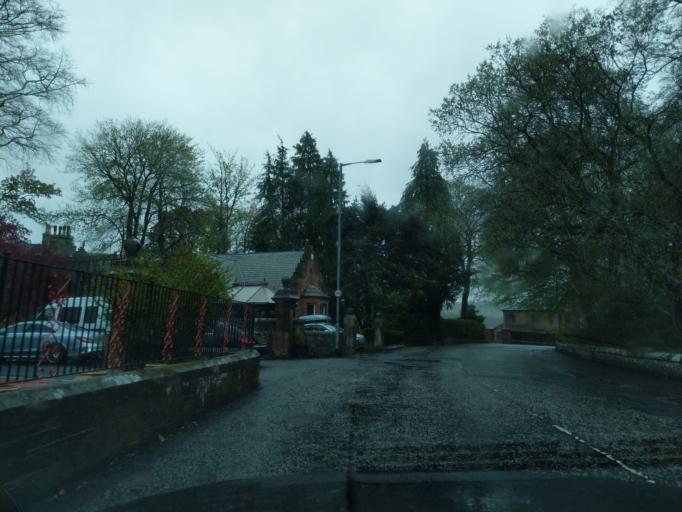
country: GB
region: Scotland
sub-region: The Scottish Borders
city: Galashiels
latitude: 55.6042
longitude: -2.7902
